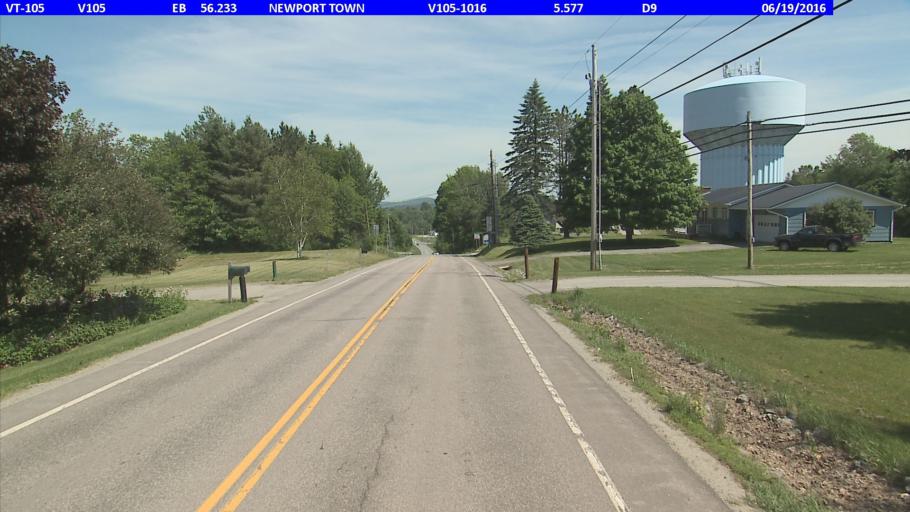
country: US
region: Vermont
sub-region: Orleans County
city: Newport
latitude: 44.9326
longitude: -72.2424
